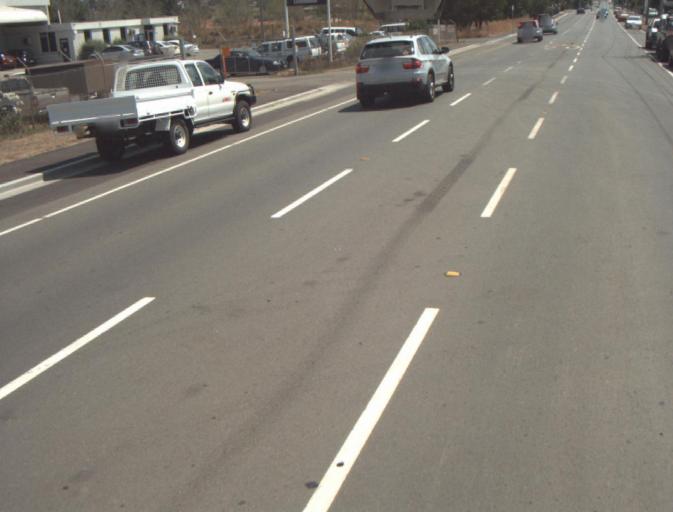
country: AU
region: Tasmania
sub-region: Launceston
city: Summerhill
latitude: -41.4890
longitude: 147.1679
